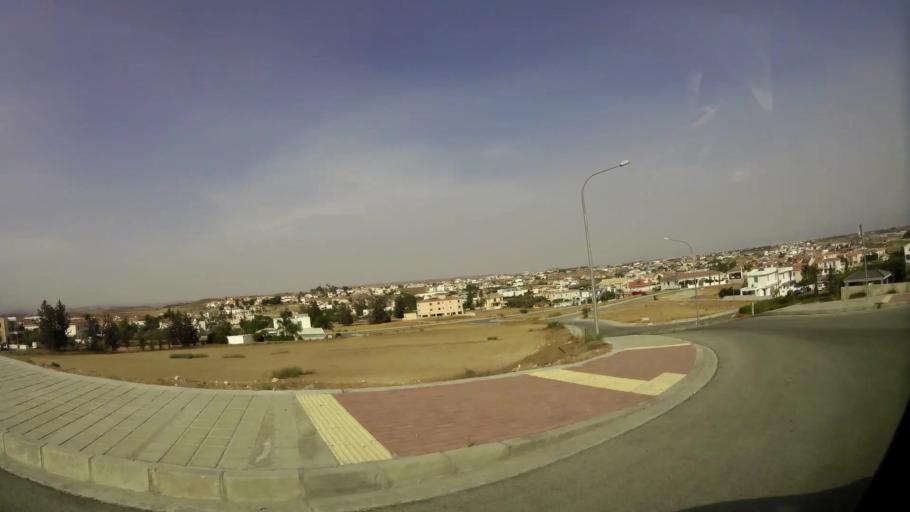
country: CY
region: Lefkosia
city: Dali
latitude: 35.0623
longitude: 33.4023
